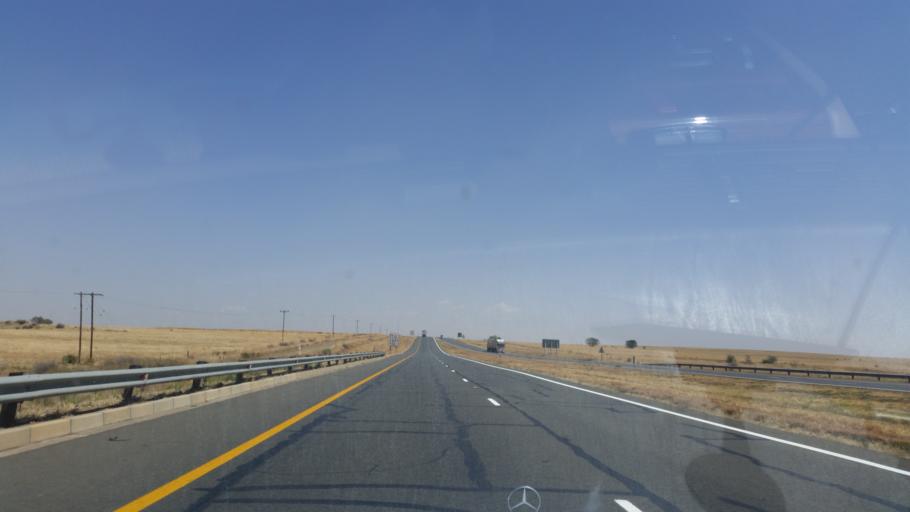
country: ZA
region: Orange Free State
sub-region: Lejweleputswa District Municipality
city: Brandfort
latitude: -28.8527
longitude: 26.5697
